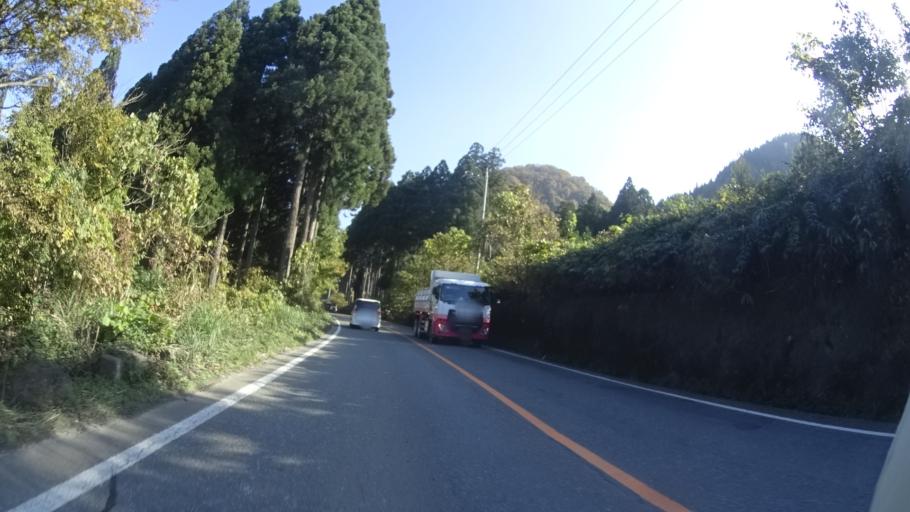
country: JP
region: Fukui
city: Ono
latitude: 35.9697
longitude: 136.5690
